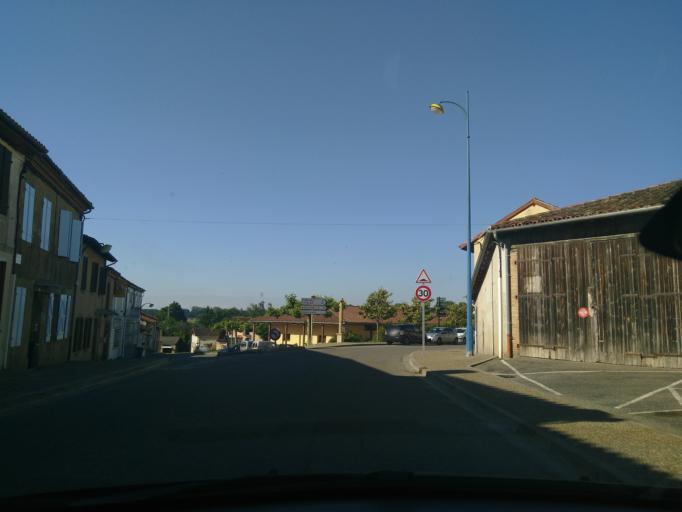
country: FR
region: Midi-Pyrenees
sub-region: Departement du Gers
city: Aubiet
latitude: 43.5218
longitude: 0.7625
